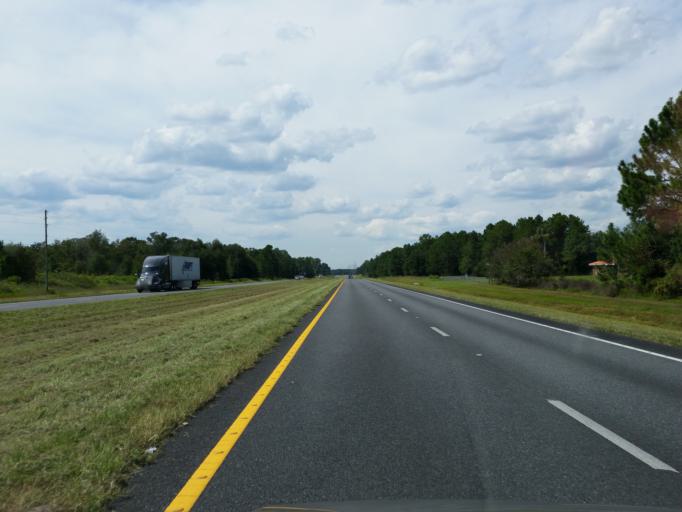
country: US
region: Florida
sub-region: Sumter County
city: Wildwood
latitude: 28.8557
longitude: -82.0700
